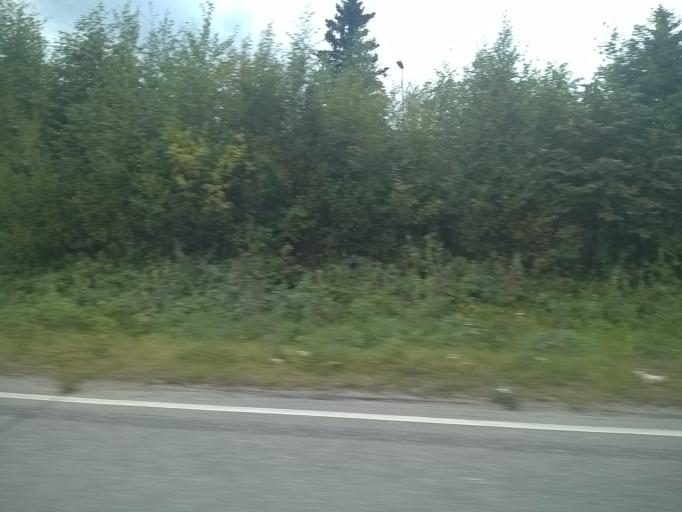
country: FI
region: Pirkanmaa
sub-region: Tampere
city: Tampere
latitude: 61.4889
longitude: 23.8239
